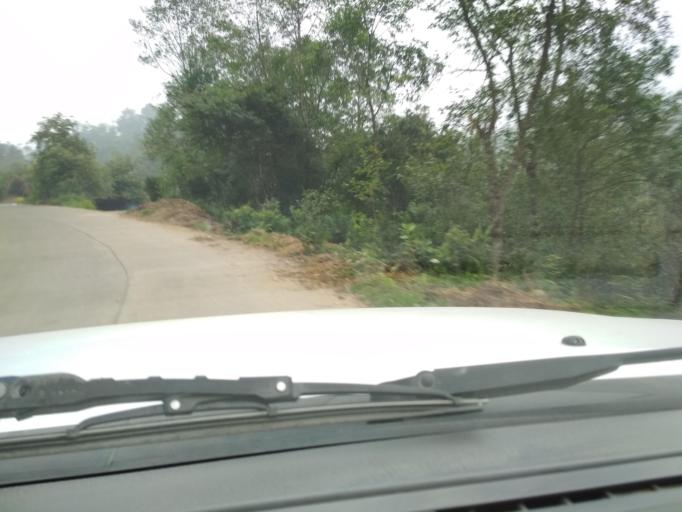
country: MX
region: Veracruz
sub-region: La Perla
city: Chilapa
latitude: 18.9745
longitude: -97.1630
